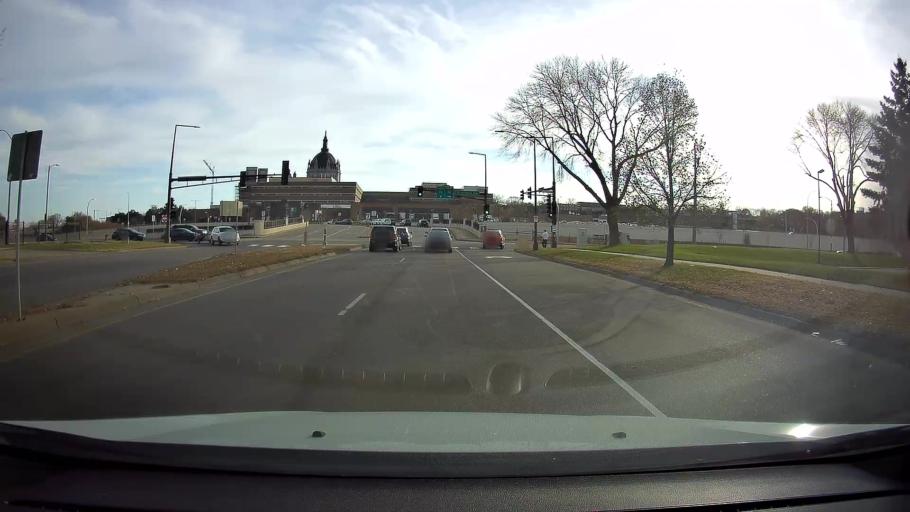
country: US
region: Minnesota
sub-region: Ramsey County
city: Saint Paul
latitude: 44.9518
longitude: -93.1100
